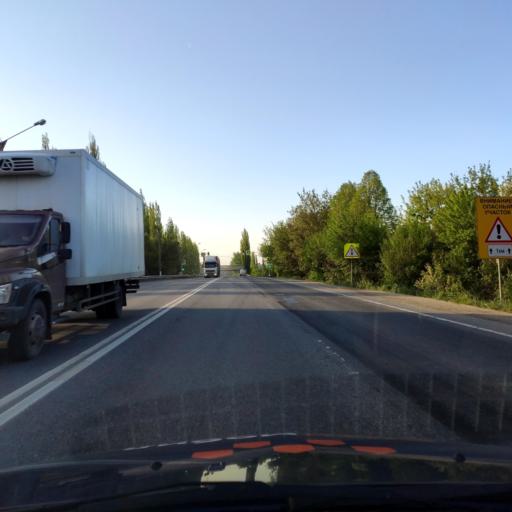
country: RU
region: Lipetsk
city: Yelets
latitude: 52.6031
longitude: 38.4700
